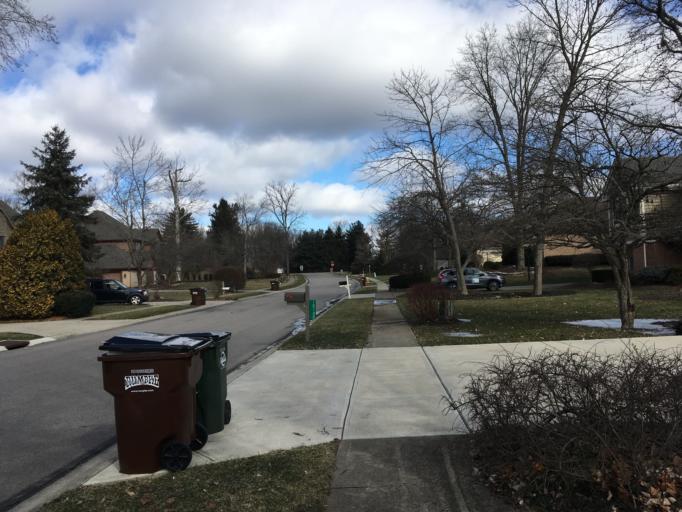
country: US
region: Ohio
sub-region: Montgomery County
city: Centerville
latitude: 39.5970
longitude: -84.1492
